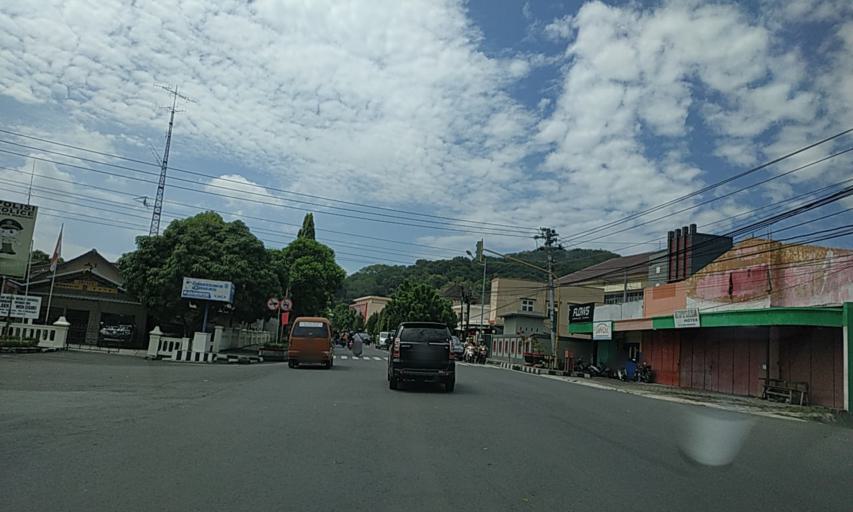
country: ID
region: Central Java
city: Selogiri
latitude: -7.8040
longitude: 110.9147
